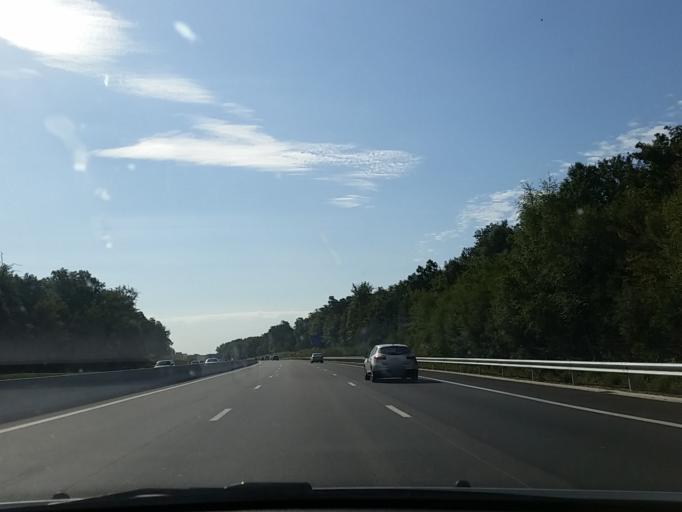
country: FR
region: Centre
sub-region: Departement du Cher
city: Vierzon
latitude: 47.2536
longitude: 2.0510
